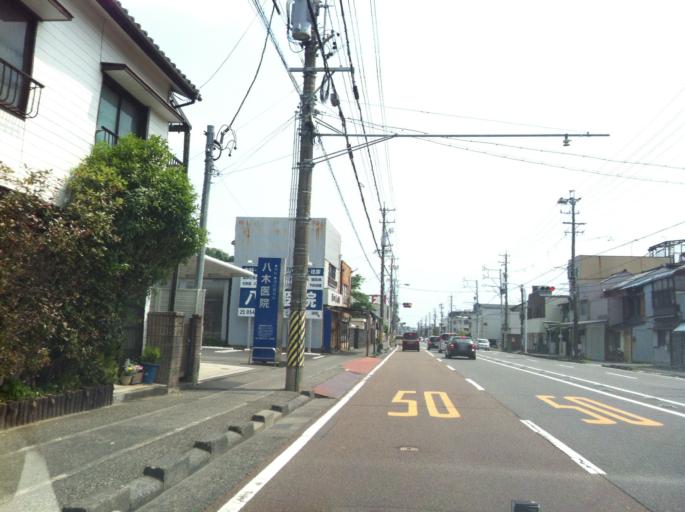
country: JP
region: Shizuoka
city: Shizuoka-shi
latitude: 34.9938
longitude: 138.3702
